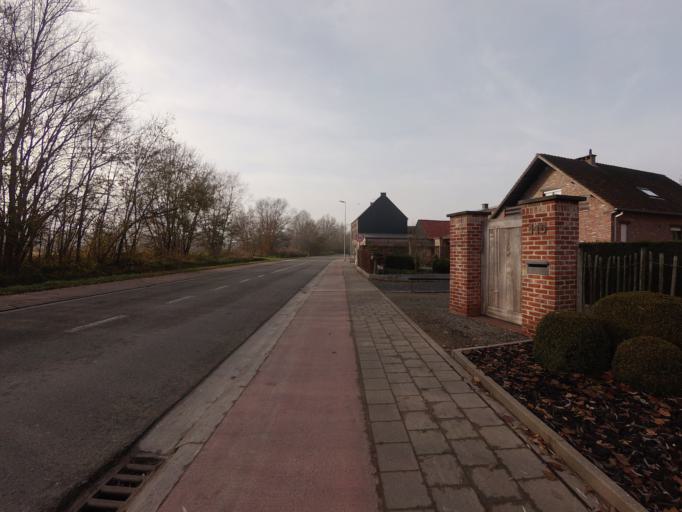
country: BE
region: Flanders
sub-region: Provincie Oost-Vlaanderen
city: Geraardsbergen
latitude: 50.7916
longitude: 3.9309
